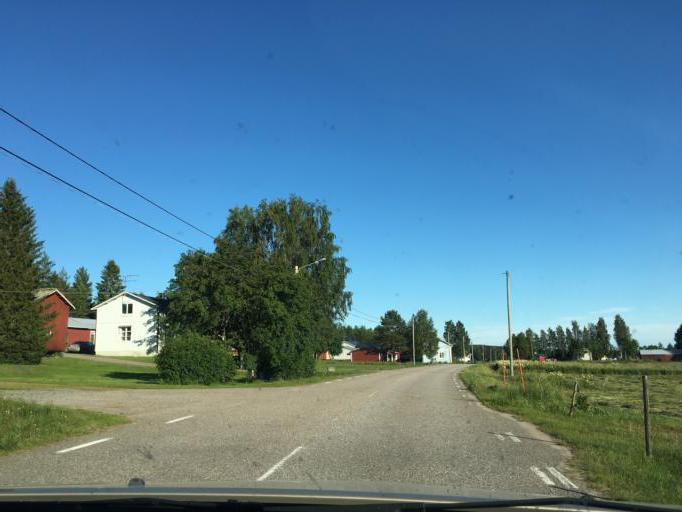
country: SE
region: Norrbotten
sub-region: Kalix Kommun
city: Rolfs
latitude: 65.9008
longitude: 22.9342
